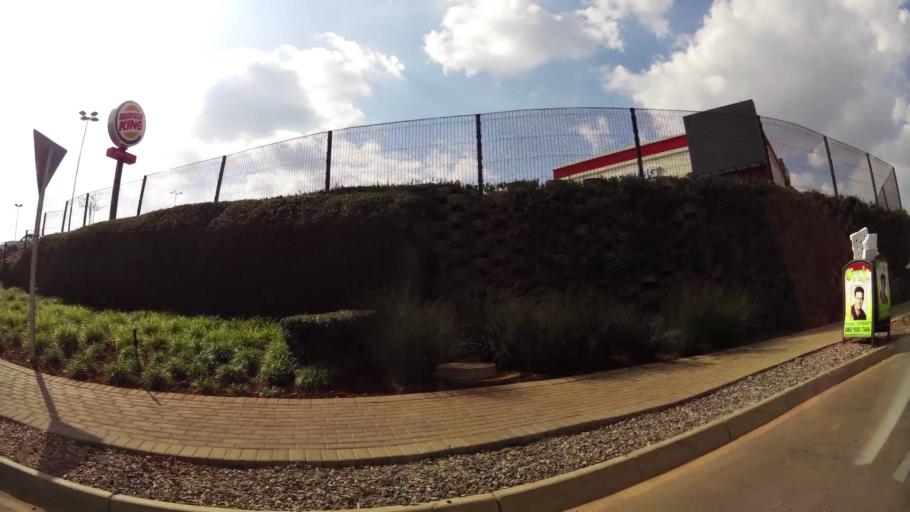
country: ZA
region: Gauteng
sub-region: City of Tshwane Metropolitan Municipality
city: Pretoria
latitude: -25.7998
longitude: 28.3328
